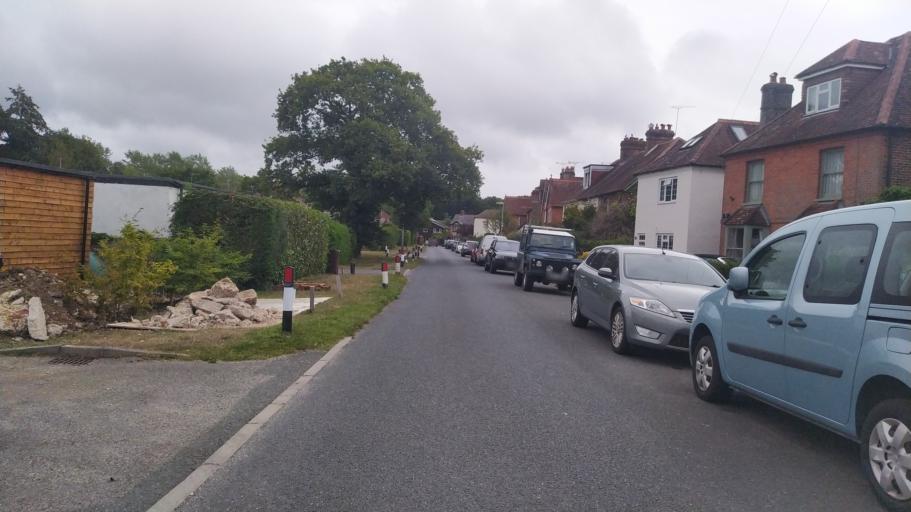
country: GB
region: England
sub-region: Hampshire
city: Havant
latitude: 50.8886
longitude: -0.9674
